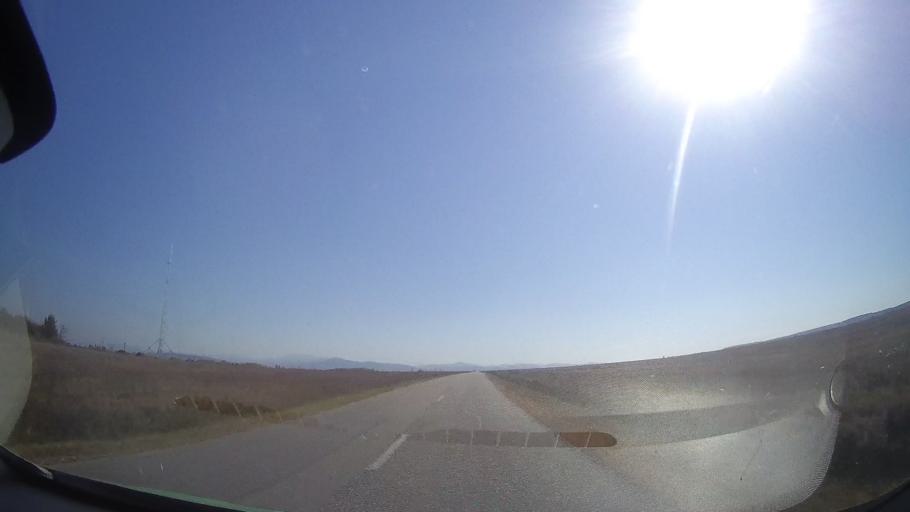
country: RO
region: Timis
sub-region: Comuna Traian Vuia
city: Traian Vuia
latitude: 45.8003
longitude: 22.0089
